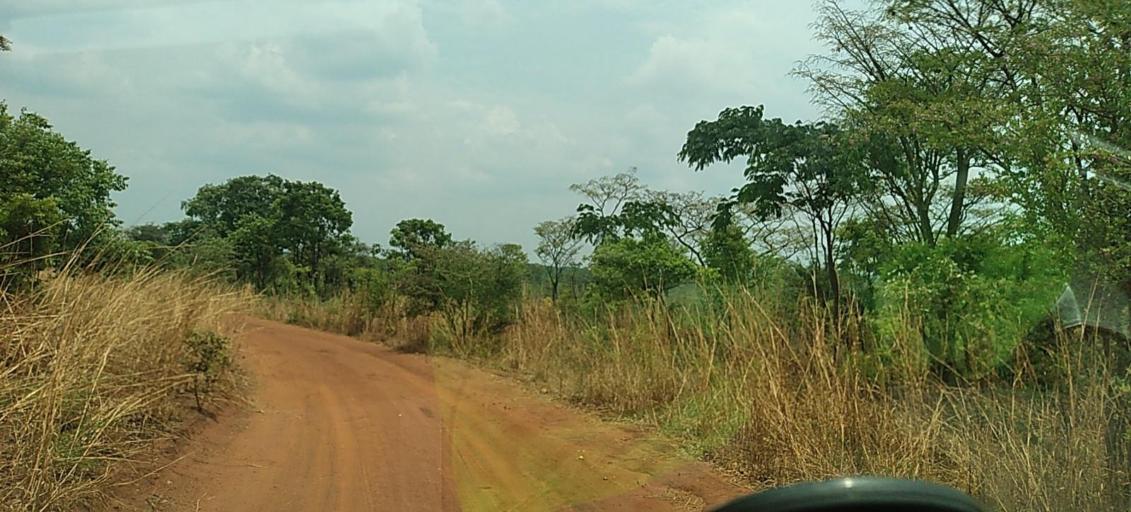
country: ZM
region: North-Western
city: Kansanshi
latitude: -12.0479
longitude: 26.3696
